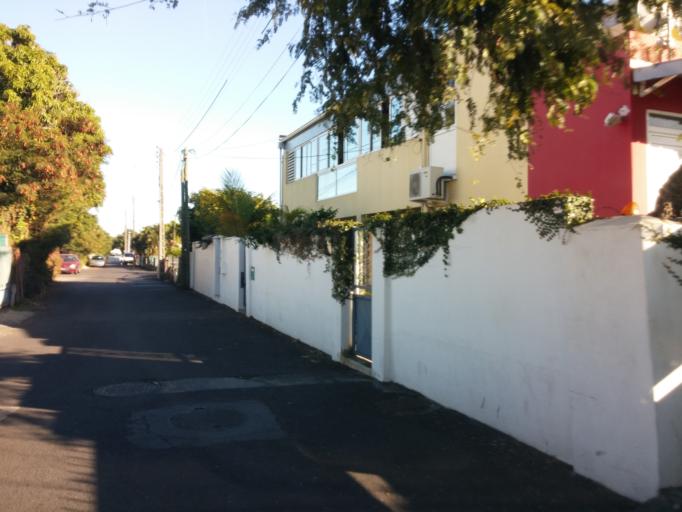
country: RE
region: Reunion
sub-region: Reunion
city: Le Port
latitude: -20.9360
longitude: 55.2956
